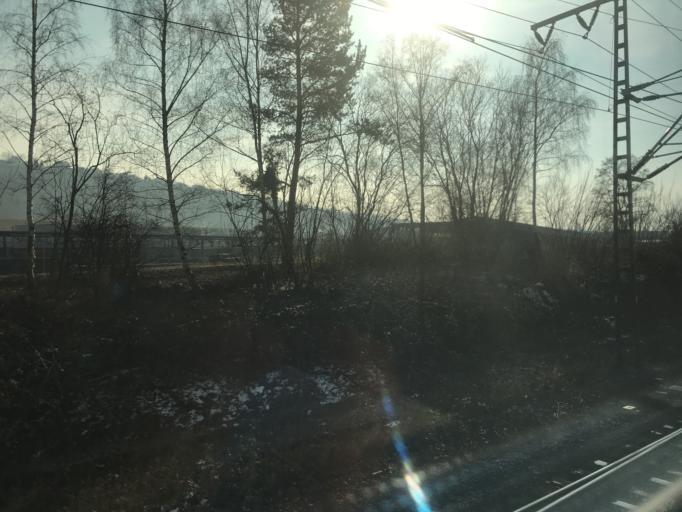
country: DE
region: Rheinland-Pfalz
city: Konz
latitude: 49.7074
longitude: 6.5877
